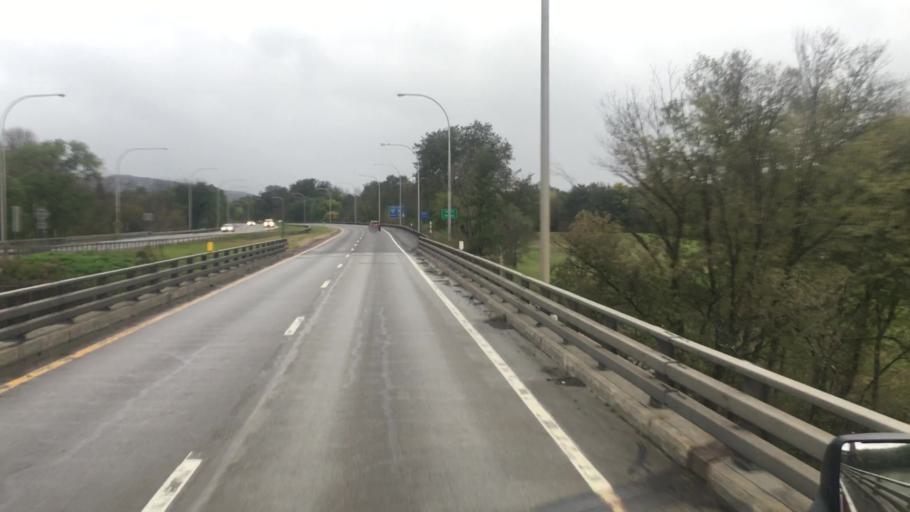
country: US
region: New York
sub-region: Broome County
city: Endwell
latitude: 42.1001
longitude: -76.0257
